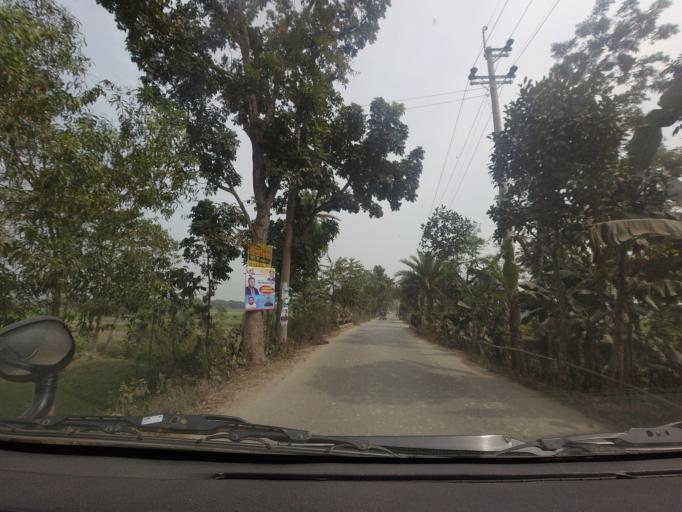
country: BD
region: Dhaka
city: Kishorganj
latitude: 24.3434
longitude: 90.7800
